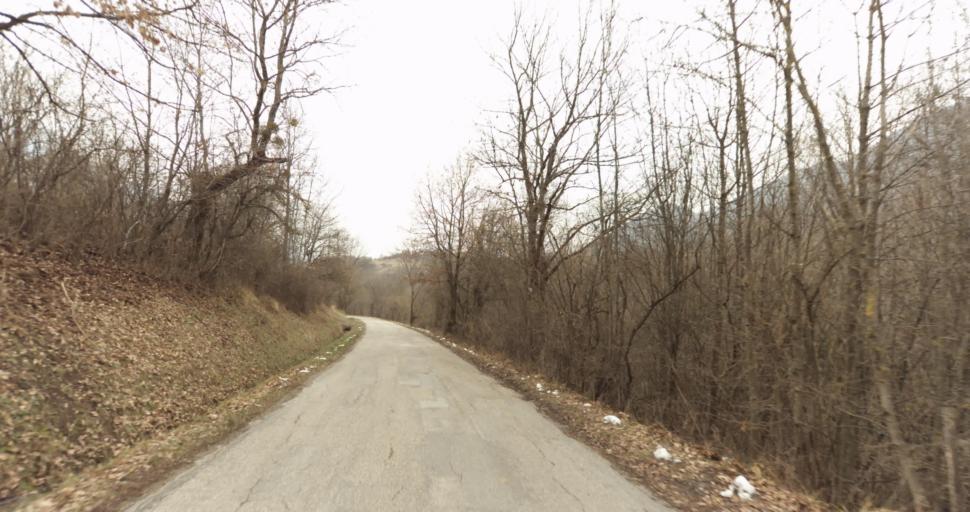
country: FR
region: Rhone-Alpes
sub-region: Departement de l'Isere
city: Vif
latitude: 45.0226
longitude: 5.6564
